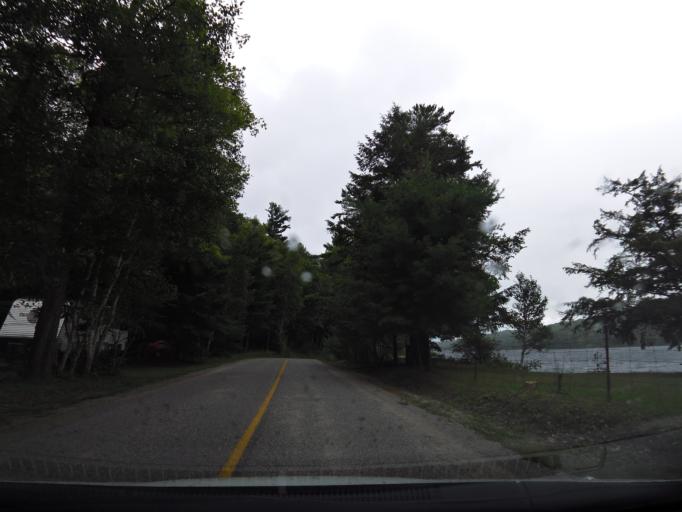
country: CA
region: Ontario
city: Perth
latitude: 44.6210
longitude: -76.5267
